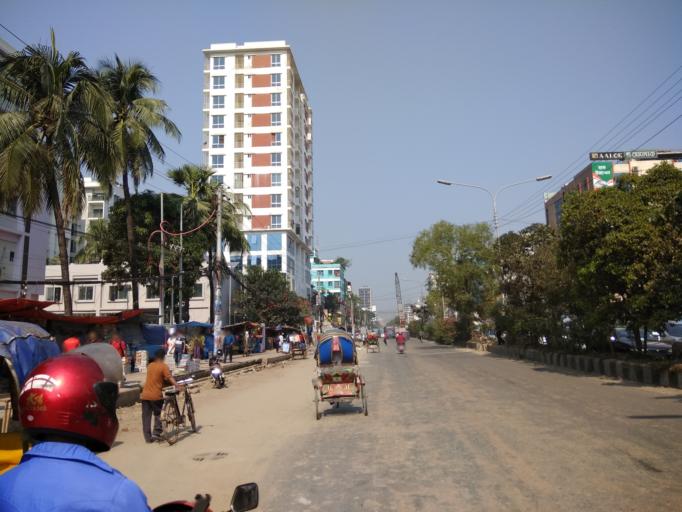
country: BD
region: Dhaka
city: Azimpur
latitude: 23.8081
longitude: 90.3682
